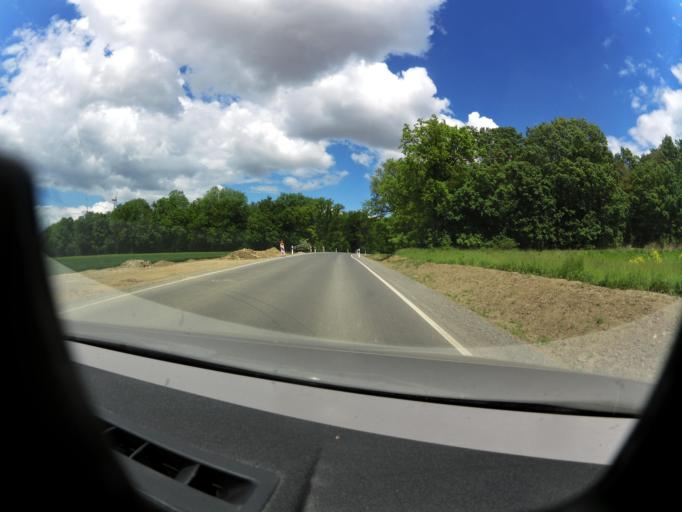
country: DE
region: Bavaria
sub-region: Regierungsbezirk Unterfranken
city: Schwanfeld
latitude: 49.9331
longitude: 10.1368
